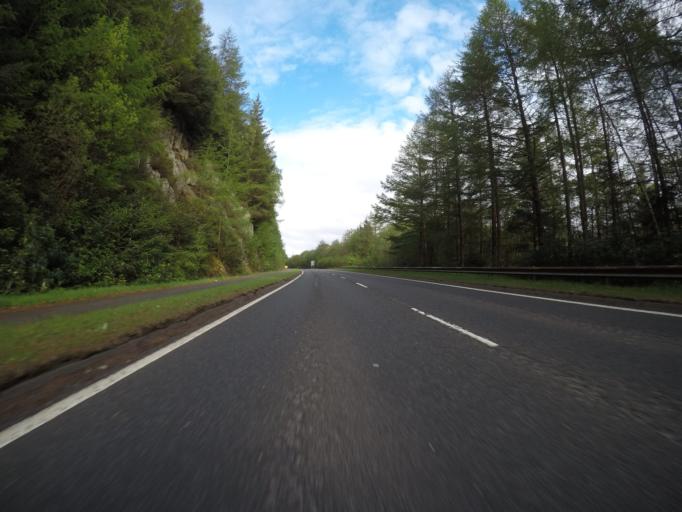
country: GB
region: Scotland
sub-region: Highland
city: Fort William
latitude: 56.6805
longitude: -5.1605
